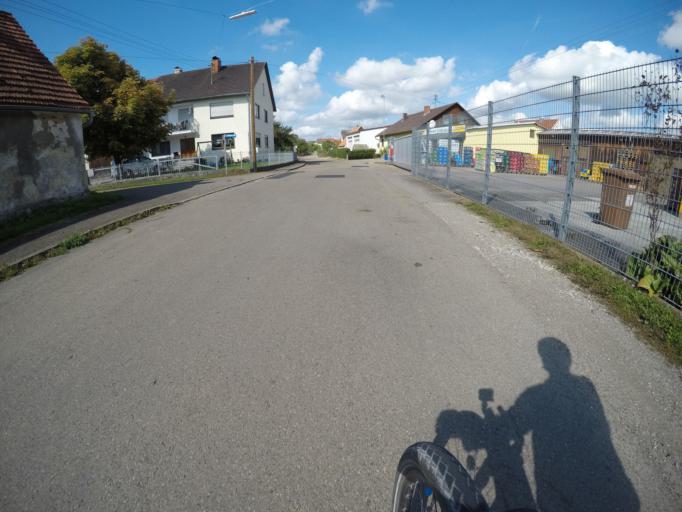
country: DE
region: Bavaria
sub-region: Swabia
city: Blindheim
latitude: 48.6328
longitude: 10.6206
